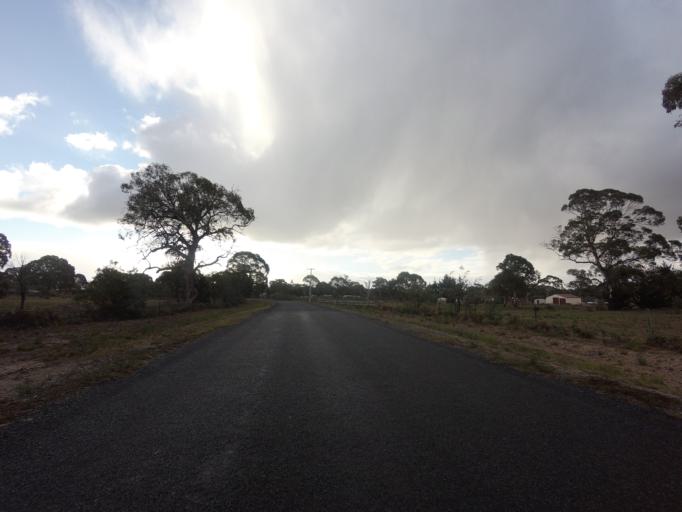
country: AU
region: Tasmania
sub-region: Break O'Day
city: St Helens
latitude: -42.1029
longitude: 148.0783
